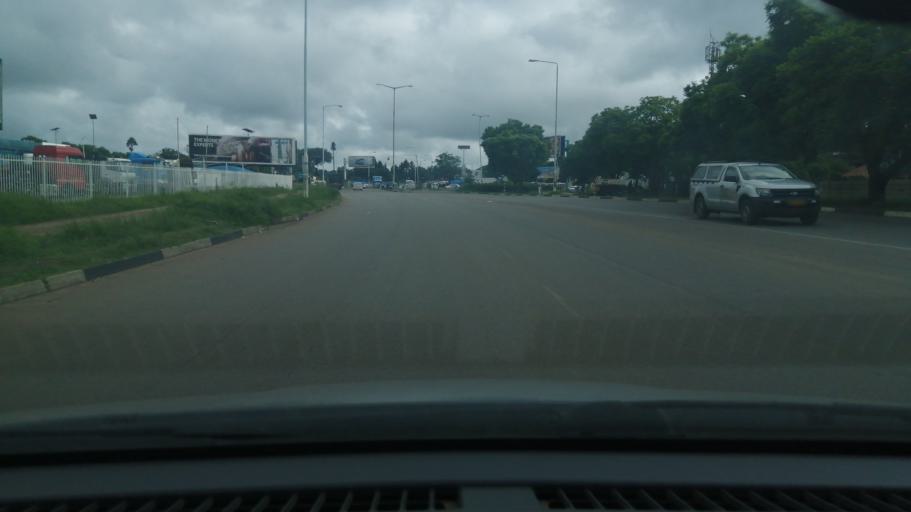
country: ZW
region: Harare
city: Harare
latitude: -17.8250
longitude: 31.0616
